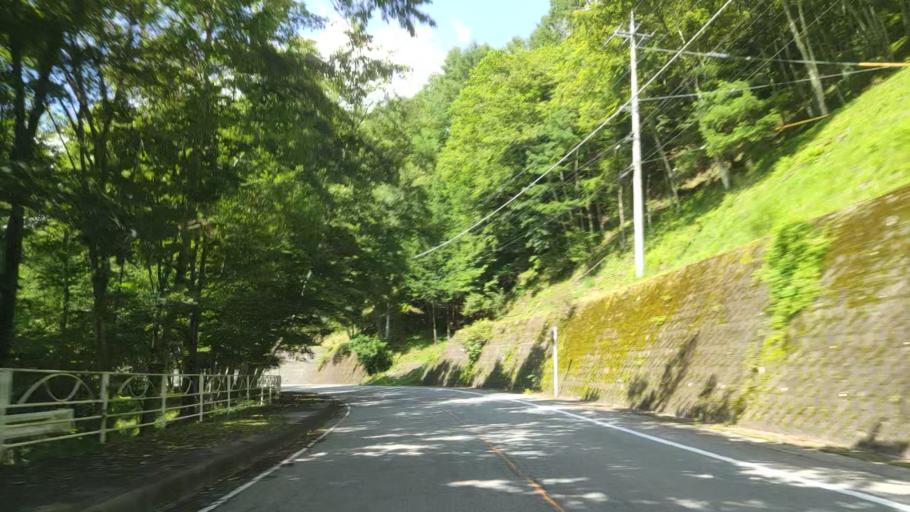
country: JP
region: Yamanashi
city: Enzan
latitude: 35.8532
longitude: 138.7585
